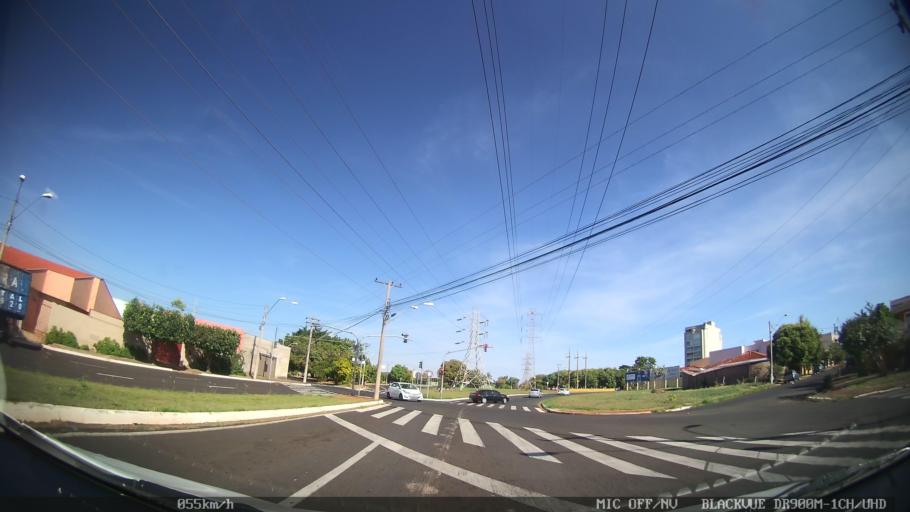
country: BR
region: Sao Paulo
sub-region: Ribeirao Preto
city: Ribeirao Preto
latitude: -21.1841
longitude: -47.7832
